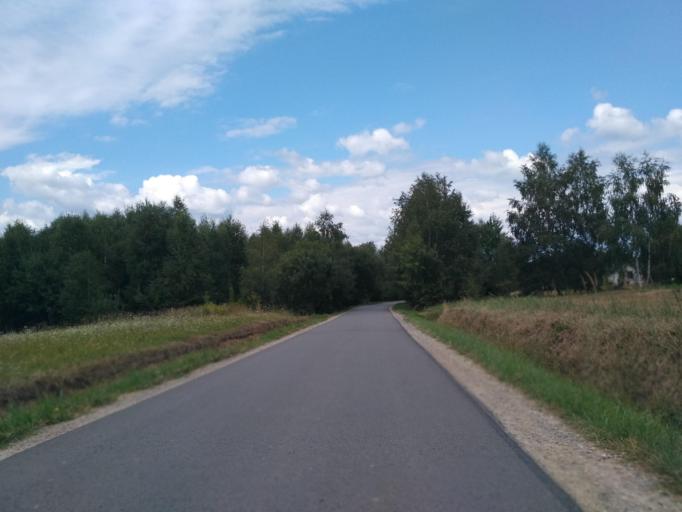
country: PL
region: Subcarpathian Voivodeship
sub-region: Powiat rzeszowski
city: Hyzne
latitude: 49.9017
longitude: 22.2273
